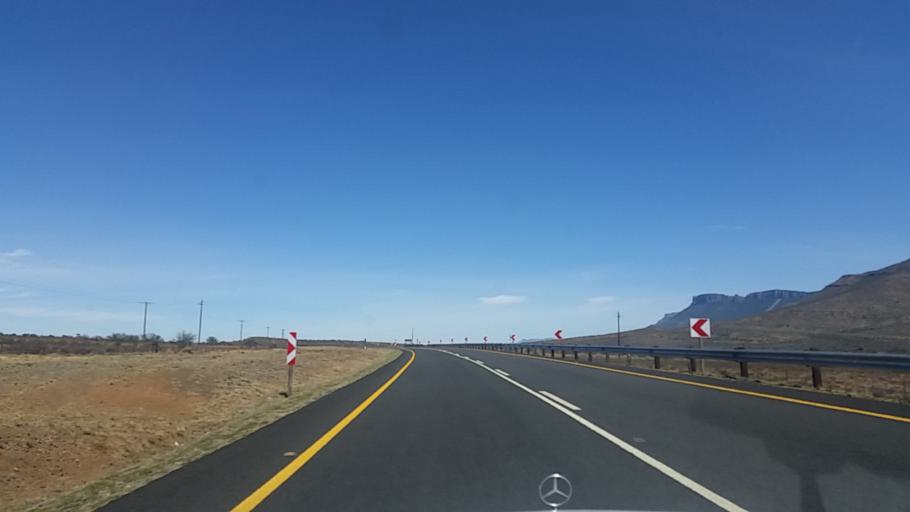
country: ZA
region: Eastern Cape
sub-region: Cacadu District Municipality
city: Graaff-Reinet
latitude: -32.3539
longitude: 24.3009
